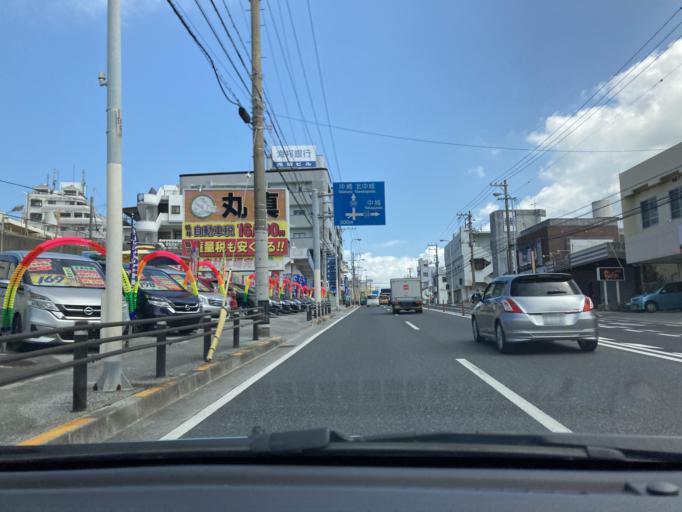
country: JP
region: Okinawa
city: Ginowan
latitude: 26.2604
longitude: 127.7594
